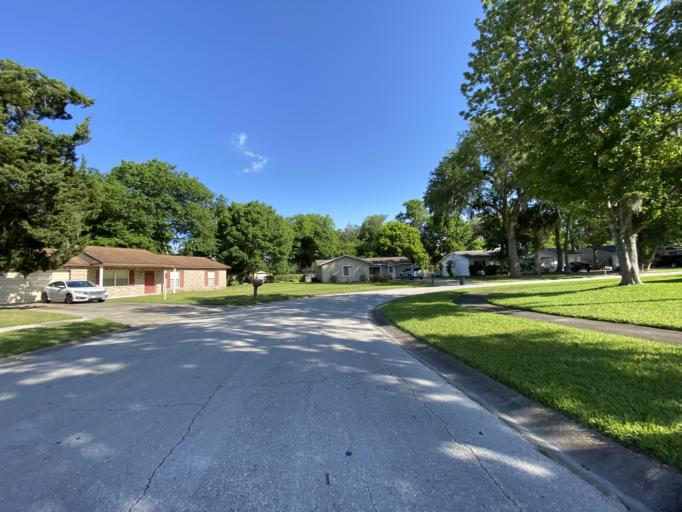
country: US
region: Florida
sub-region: Volusia County
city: South Daytona
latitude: 29.1746
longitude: -81.0166
